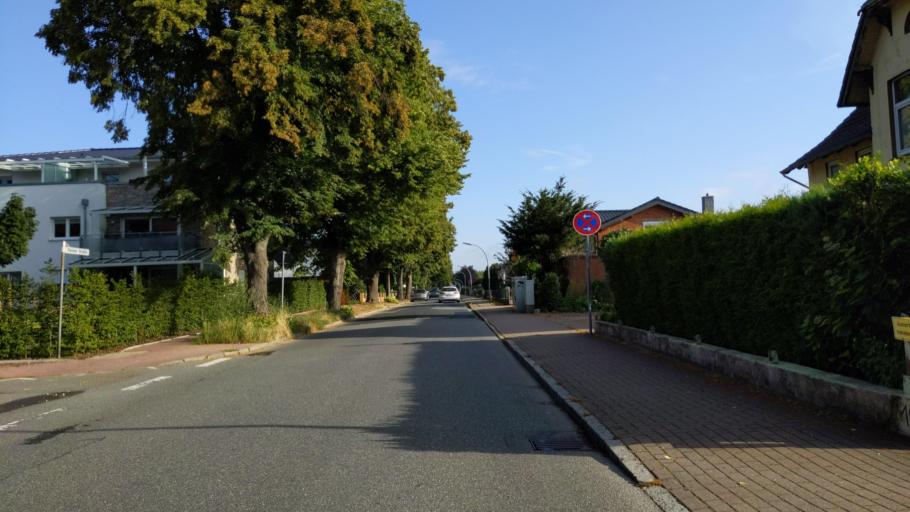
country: DE
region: Schleswig-Holstein
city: Bad Schwartau
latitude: 53.9255
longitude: 10.6927
